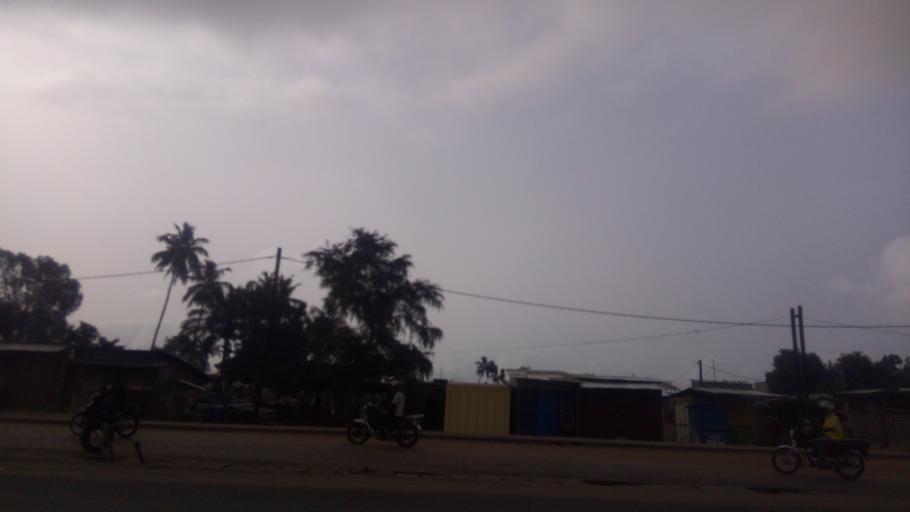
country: BJ
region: Atlantique
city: Abomey-Calavi
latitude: 6.3883
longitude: 2.3509
